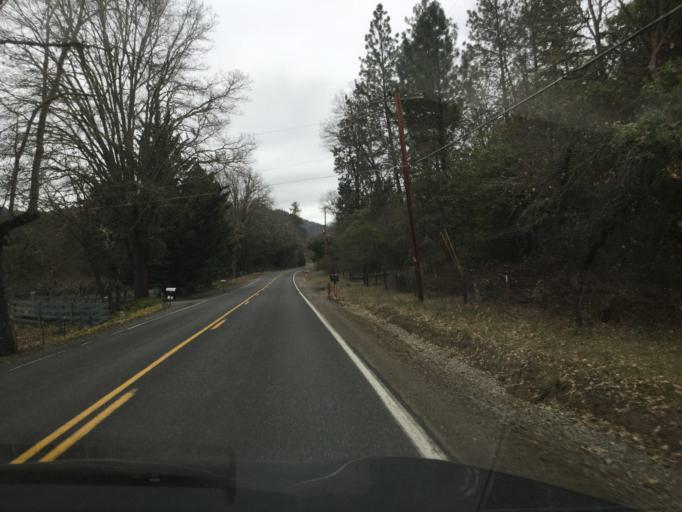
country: US
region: Oregon
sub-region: Jackson County
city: Gold Hill
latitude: 42.4028
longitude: -123.0265
